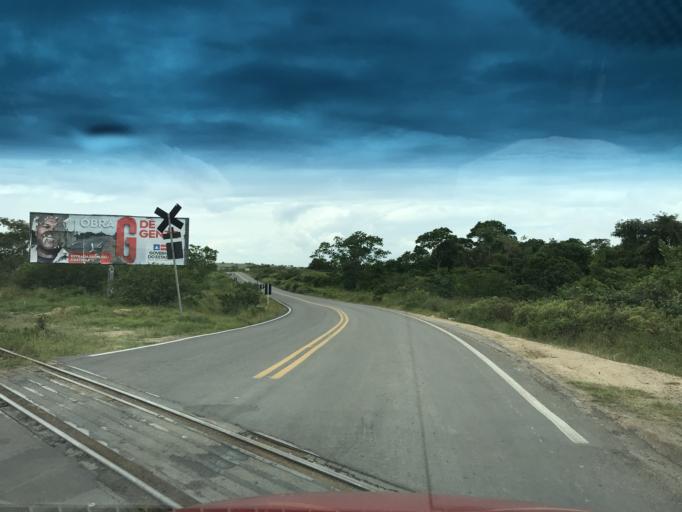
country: BR
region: Bahia
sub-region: Castro Alves
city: Castro Alves
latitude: -12.7572
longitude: -39.4158
